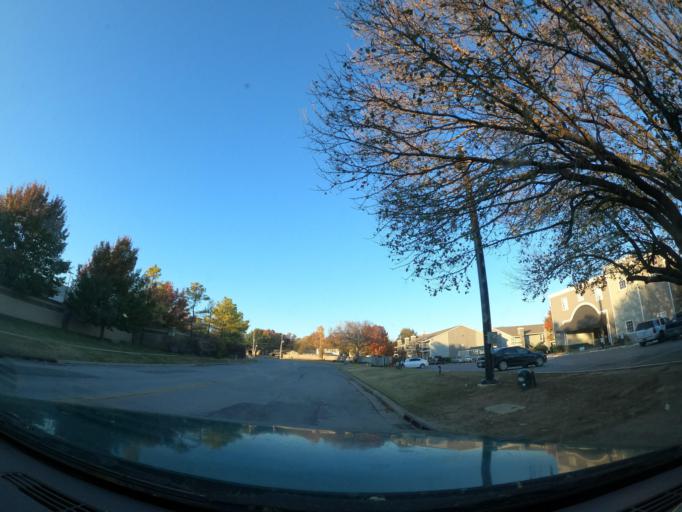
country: US
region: Oklahoma
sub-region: Tulsa County
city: Broken Arrow
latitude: 36.0669
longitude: -95.8815
